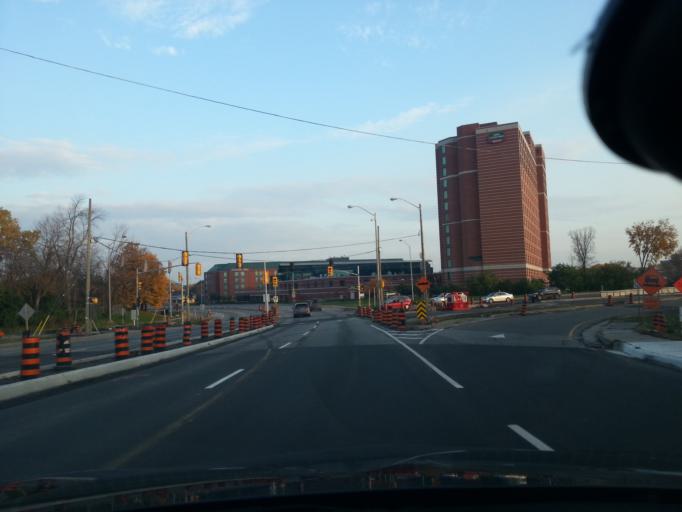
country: CA
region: Ontario
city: Ottawa
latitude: 45.4187
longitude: -75.6566
